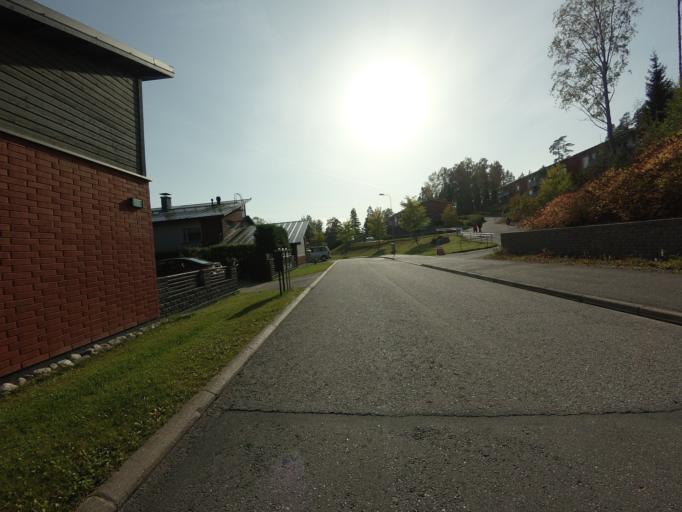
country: FI
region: Uusimaa
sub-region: Helsinki
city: Espoo
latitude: 60.1720
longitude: 24.6437
